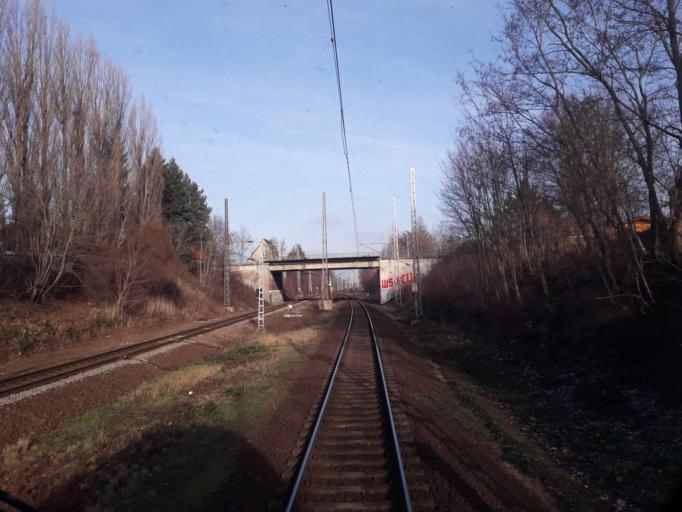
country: DE
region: Berlin
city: Altglienicke
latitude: 52.4132
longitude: 13.5524
